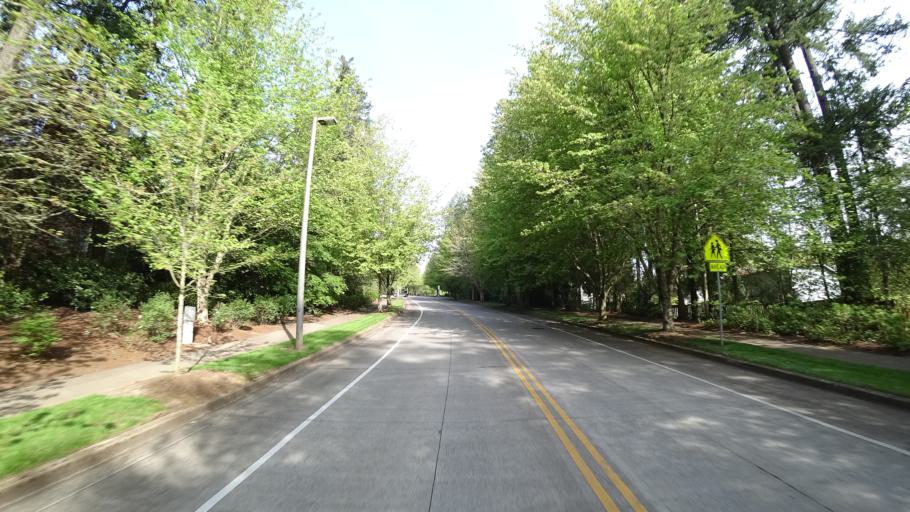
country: US
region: Oregon
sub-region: Washington County
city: King City
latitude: 45.4447
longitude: -122.8402
